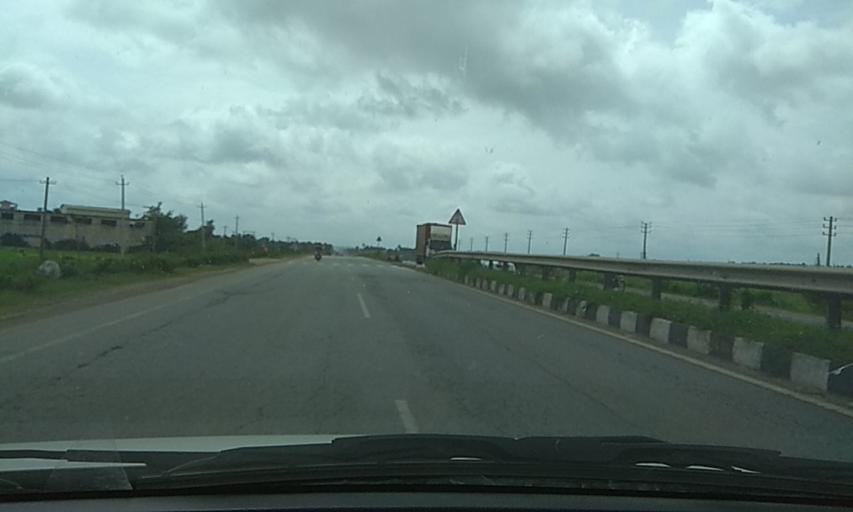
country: IN
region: Karnataka
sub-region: Davanagere
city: Harihar
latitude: 14.4550
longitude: 75.8681
